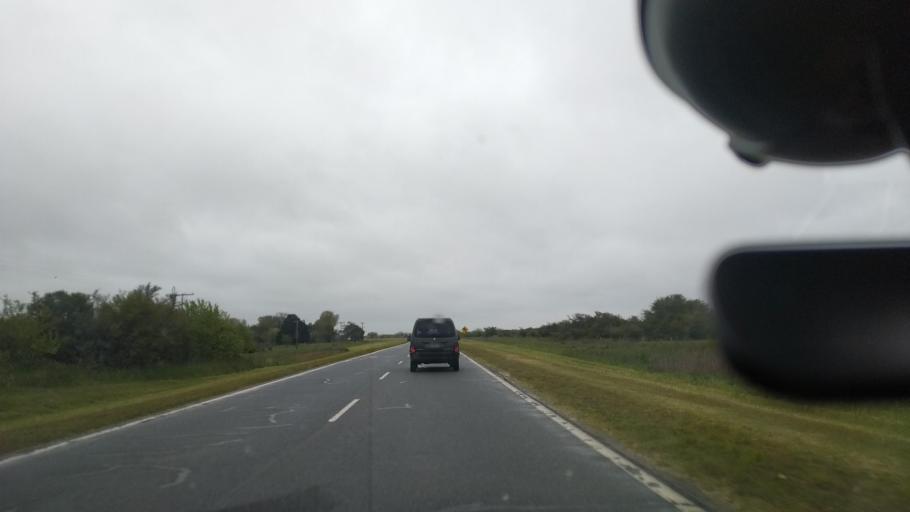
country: AR
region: Buenos Aires
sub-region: Partido de Castelli
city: Castelli
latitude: -35.9403
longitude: -57.4467
